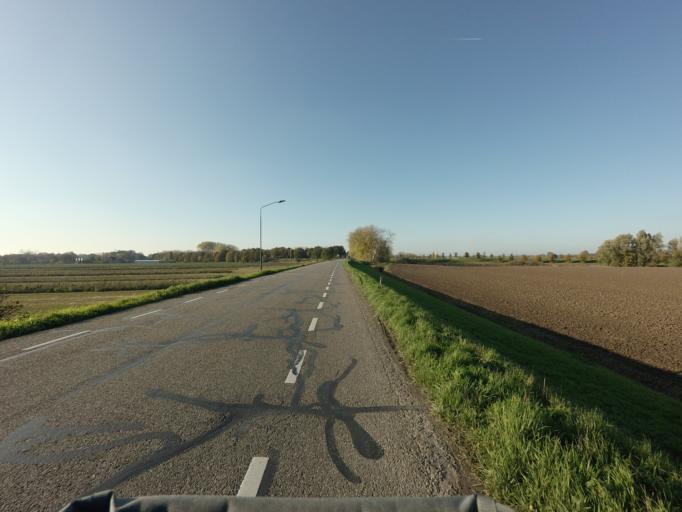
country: NL
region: North Brabant
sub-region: Gemeente Woudrichem
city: Woudrichem
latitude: 51.7894
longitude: 5.0441
